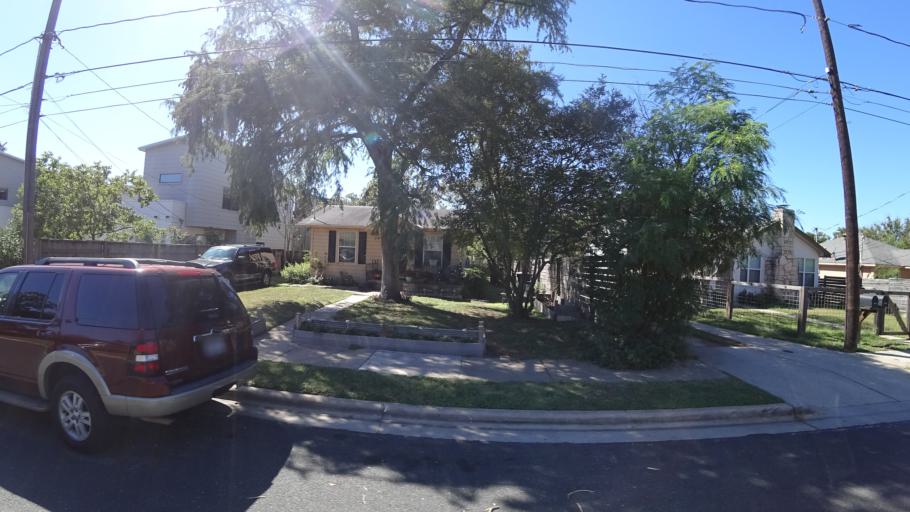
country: US
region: Texas
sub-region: Travis County
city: Austin
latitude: 30.2813
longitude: -97.7054
